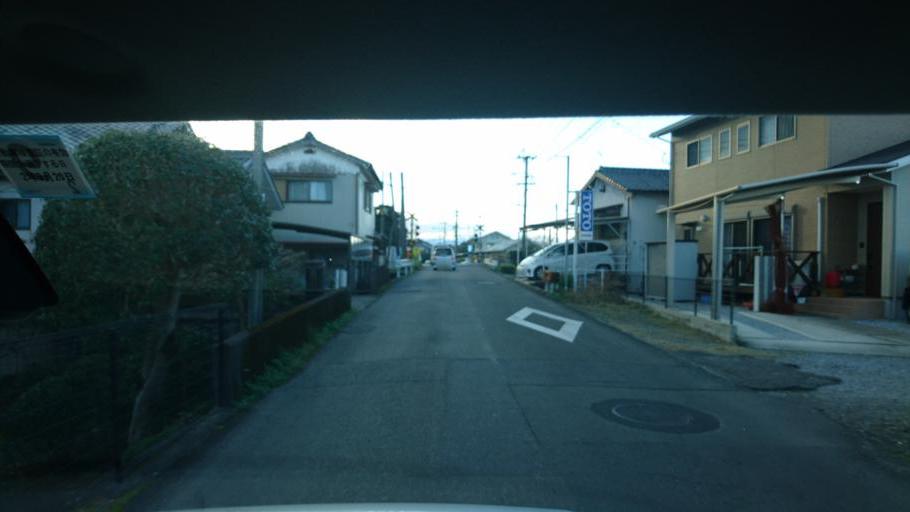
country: JP
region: Miyazaki
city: Miyazaki-shi
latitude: 31.8336
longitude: 131.4353
